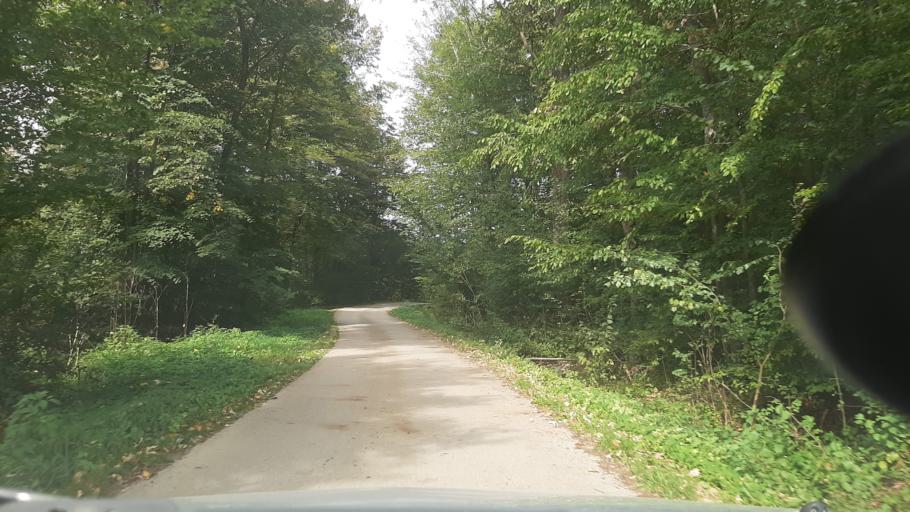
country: BA
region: Republika Srpska
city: Maglajani
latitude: 44.8702
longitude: 17.4697
